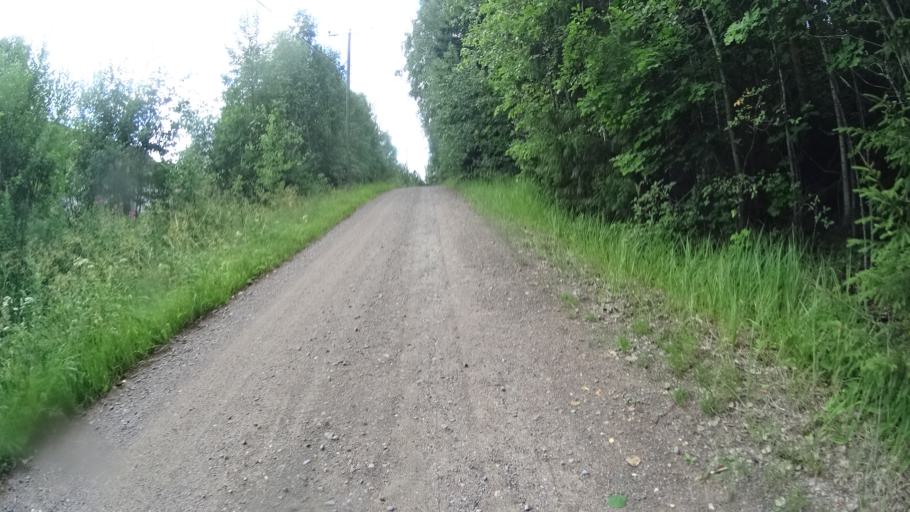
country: FI
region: Uusimaa
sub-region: Helsinki
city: Karkkila
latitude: 60.6062
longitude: 24.1932
